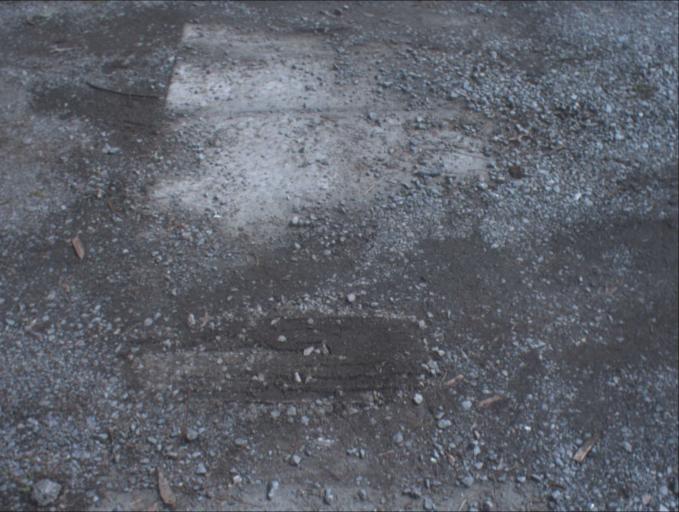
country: AU
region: Queensland
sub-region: Logan
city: Park Ridge South
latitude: -27.7175
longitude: 152.9804
